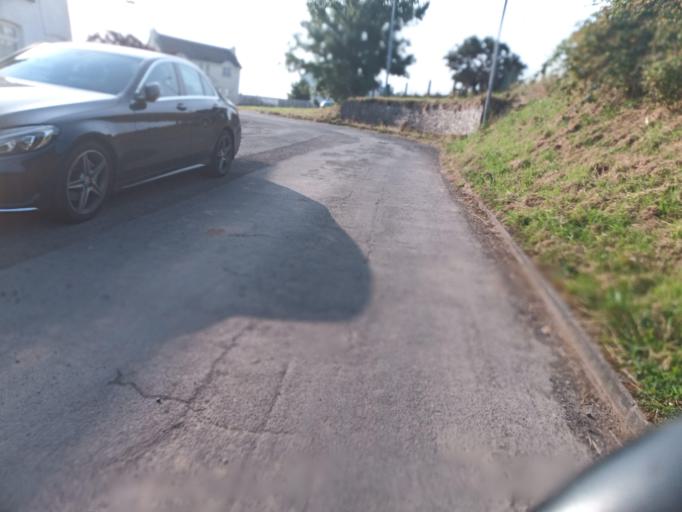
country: GB
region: Northern Ireland
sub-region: Ards District
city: Comber
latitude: 54.5580
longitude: -5.7585
